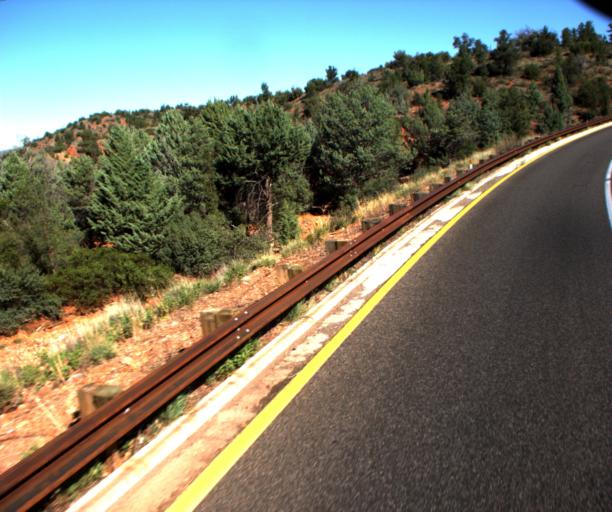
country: US
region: Arizona
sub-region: Yavapai County
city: Village of Oak Creek (Big Park)
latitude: 34.8189
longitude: -111.7722
